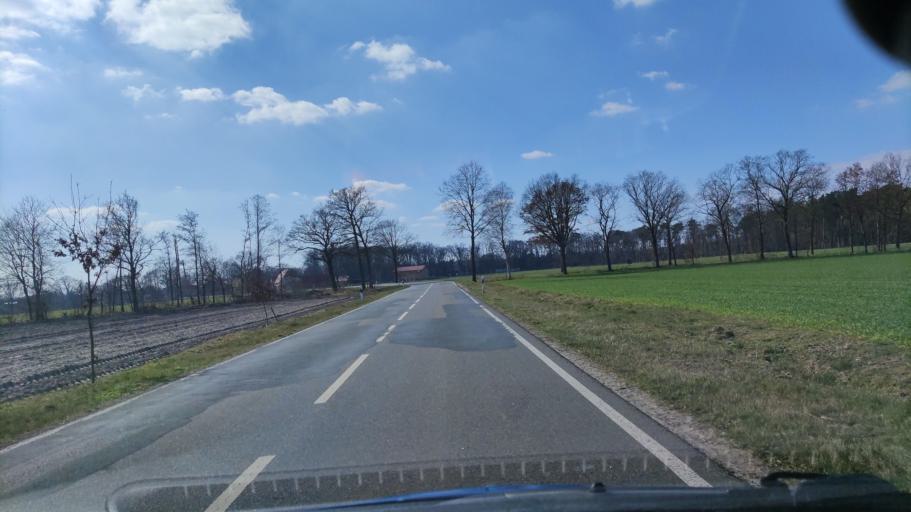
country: DE
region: Lower Saxony
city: Trebel
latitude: 53.0309
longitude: 11.2757
